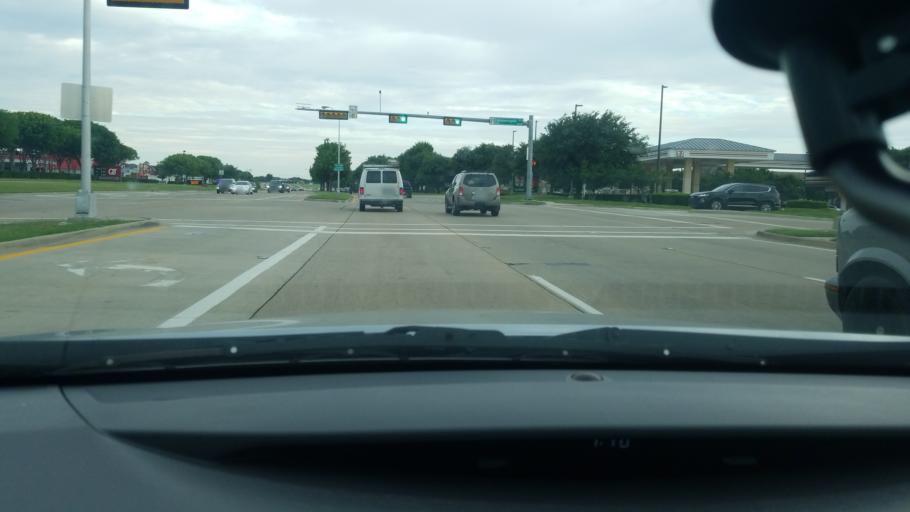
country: US
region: Texas
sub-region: Collin County
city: Frisco
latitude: 33.0613
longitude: -96.7963
